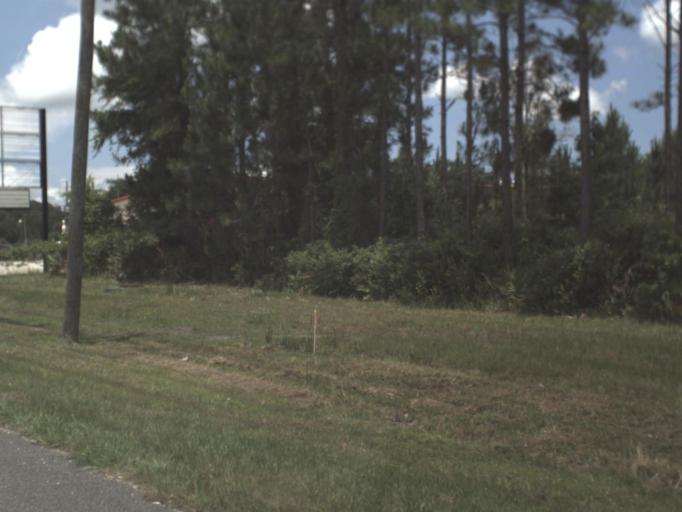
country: US
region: Florida
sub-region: Nassau County
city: Yulee
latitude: 30.6277
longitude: -81.5999
